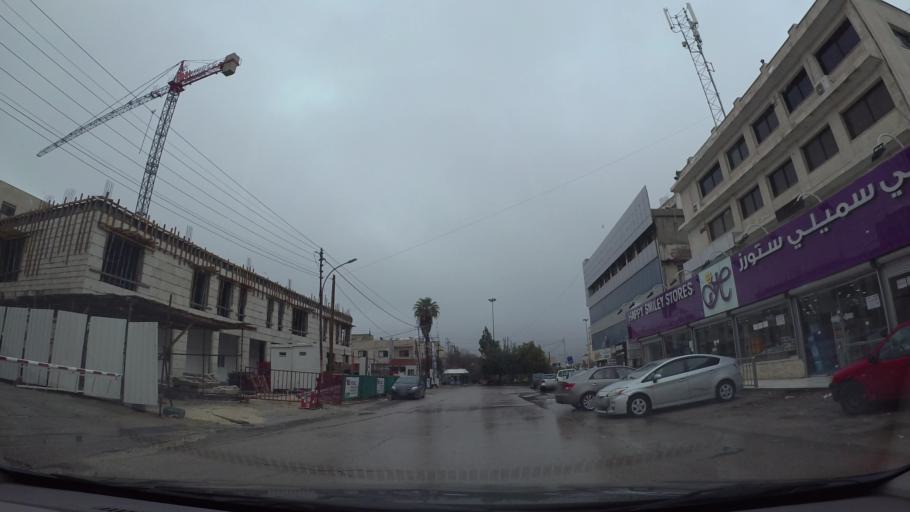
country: JO
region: Amman
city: Wadi as Sir
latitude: 31.9610
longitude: 35.8579
